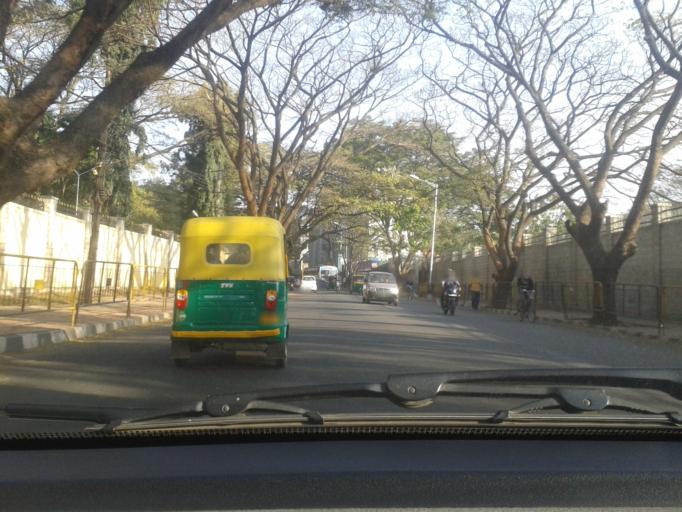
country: IN
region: Karnataka
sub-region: Bangalore Urban
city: Bangalore
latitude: 13.0262
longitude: 77.5719
